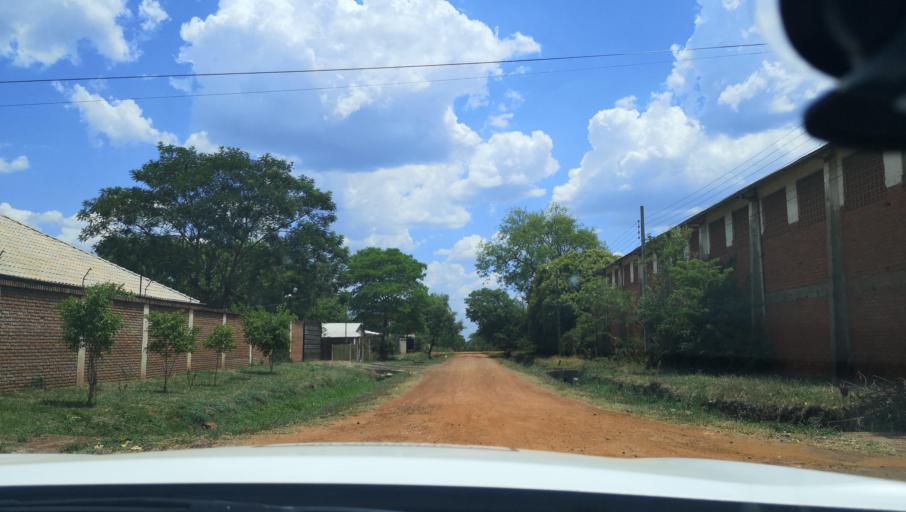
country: PY
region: Itapua
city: Carmen del Parana
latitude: -27.1675
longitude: -56.2359
